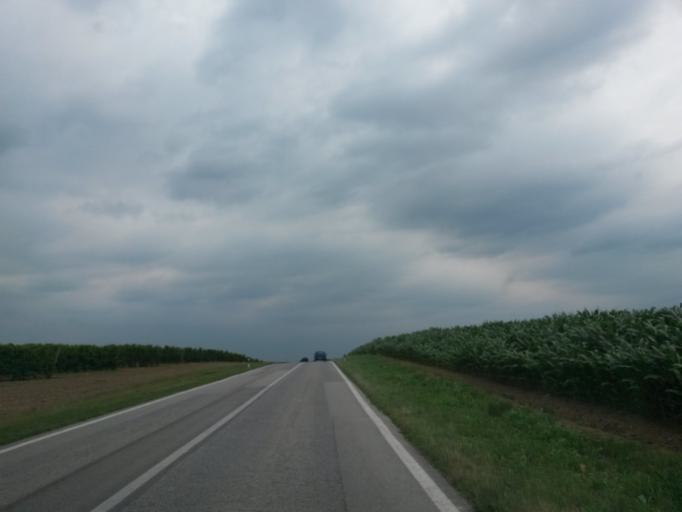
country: HR
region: Vukovarsko-Srijemska
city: Vukovar
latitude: 45.3264
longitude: 19.0562
